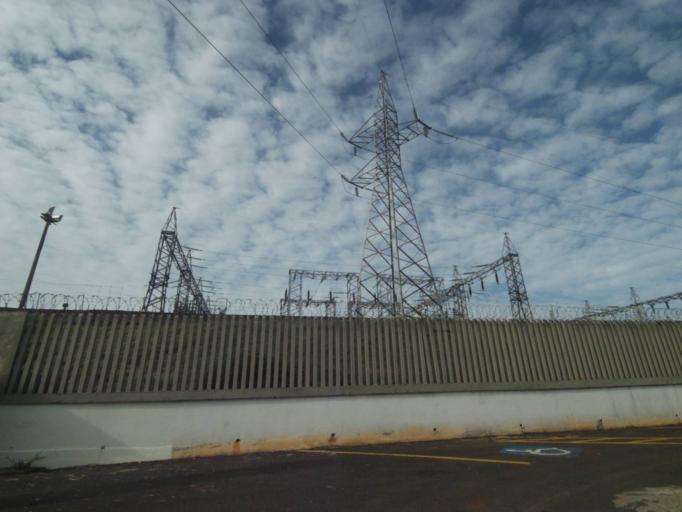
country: BR
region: Parana
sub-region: Telemaco Borba
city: Telemaco Borba
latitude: -24.3392
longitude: -50.6099
